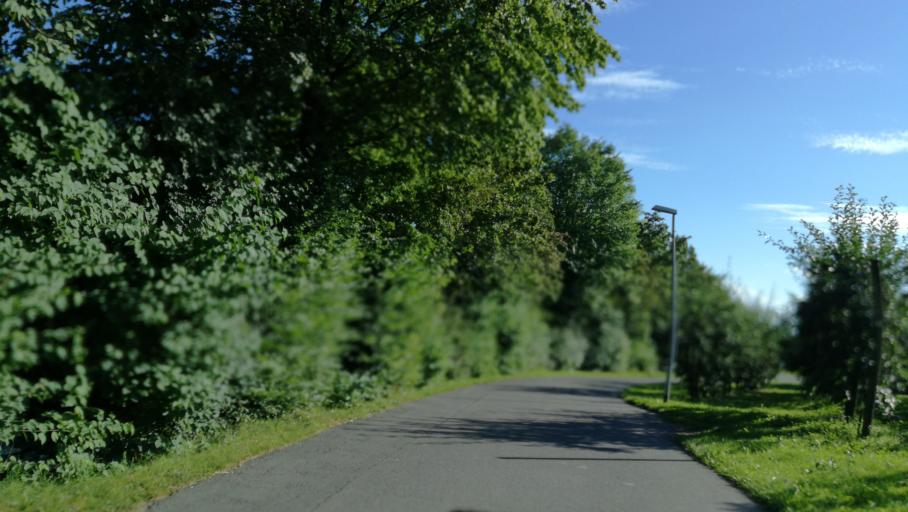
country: CH
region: Zug
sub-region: Zug
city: Zug
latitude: 47.1803
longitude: 8.5016
